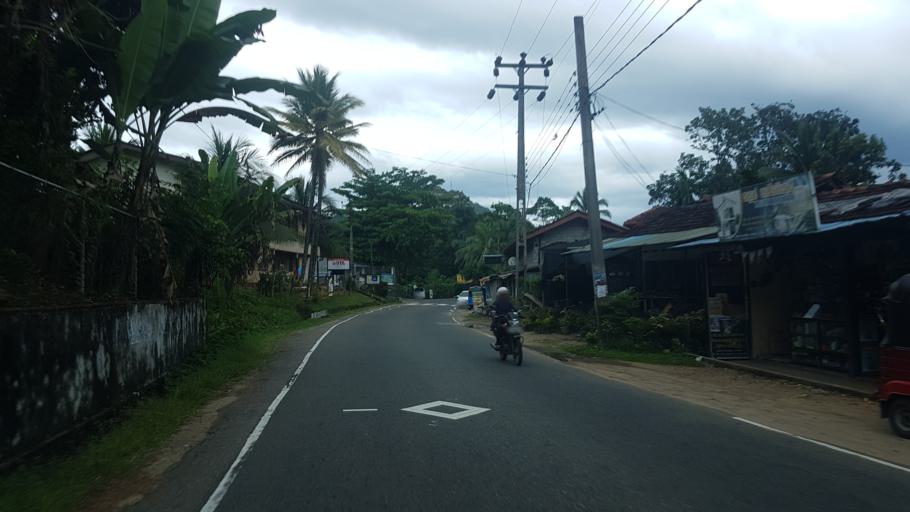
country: LK
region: Western
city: Hanwella Ihala
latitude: 7.0298
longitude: 80.2828
